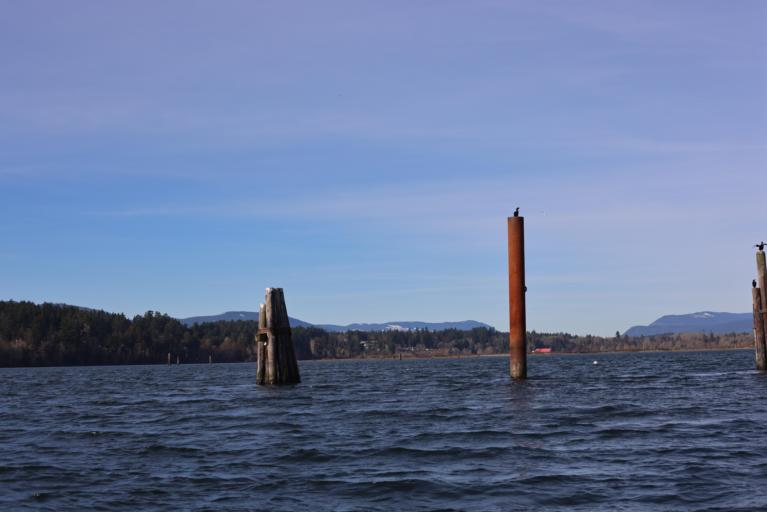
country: CA
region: British Columbia
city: Duncan
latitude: 48.7465
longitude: -123.6229
